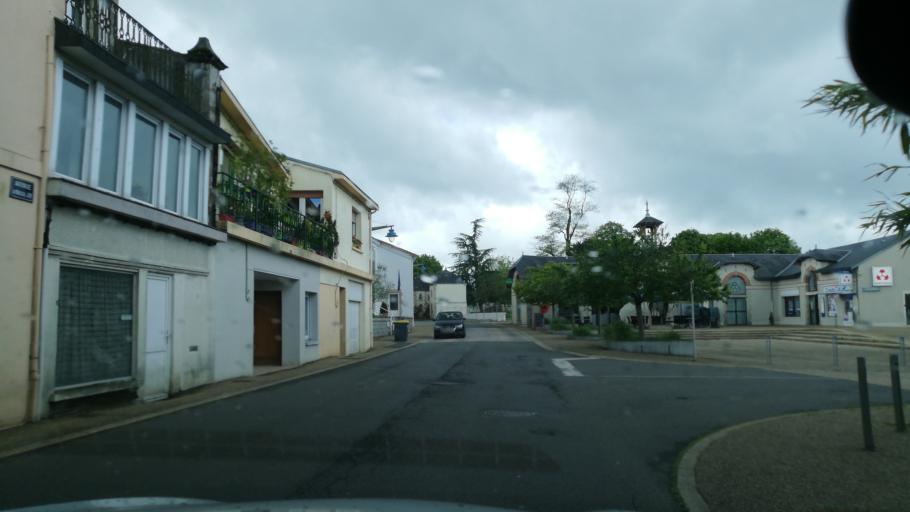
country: FR
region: Poitou-Charentes
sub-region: Departement des Deux-Sevres
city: Moncoutant
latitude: 46.7216
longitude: -0.5884
